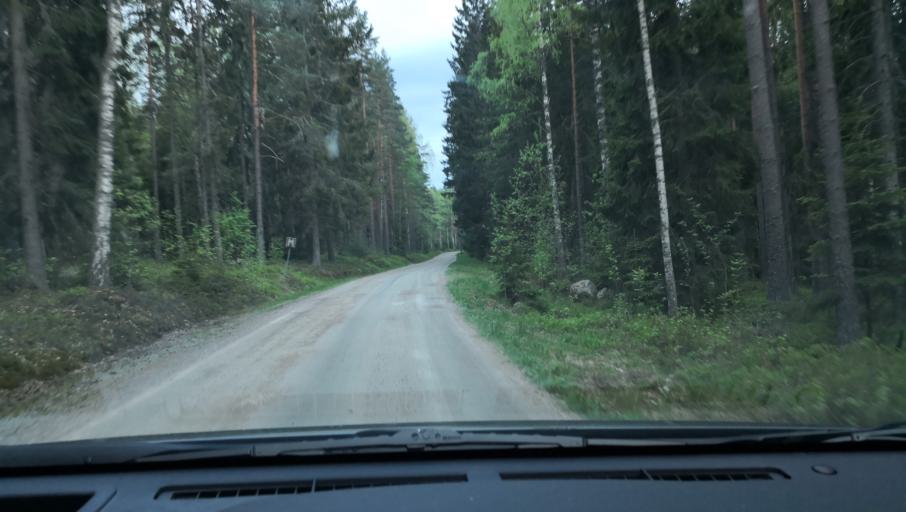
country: SE
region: Vaestmanland
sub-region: Skinnskattebergs Kommun
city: Skinnskatteberg
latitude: 59.7396
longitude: 15.4699
